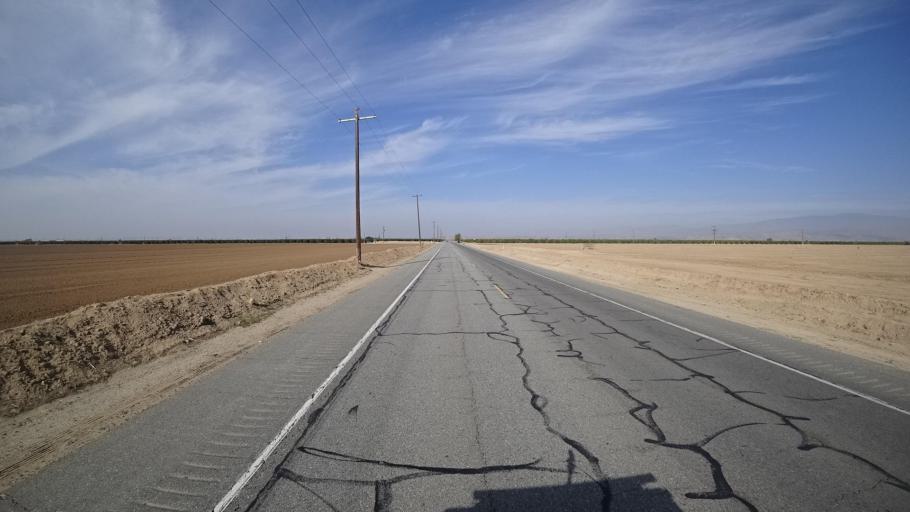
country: US
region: California
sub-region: Kern County
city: Lamont
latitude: 35.3123
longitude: -118.8430
